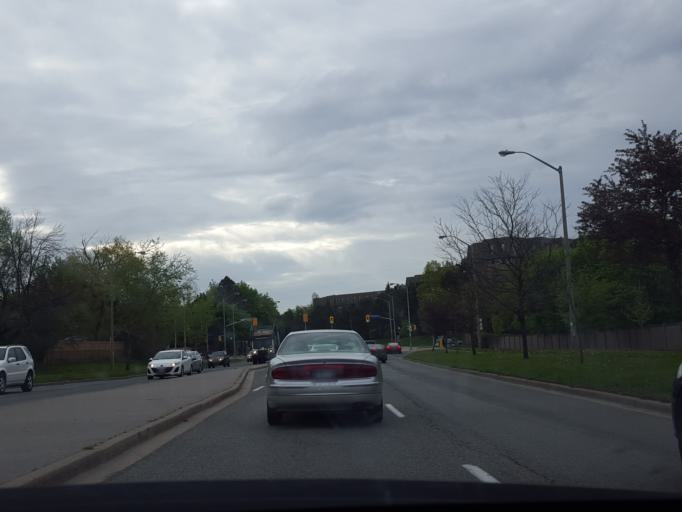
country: CA
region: Ontario
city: Willowdale
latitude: 43.7943
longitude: -79.3385
